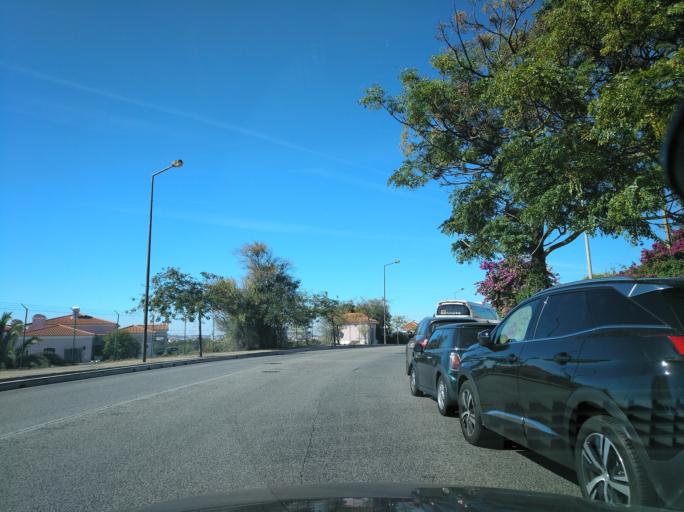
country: PT
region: Lisbon
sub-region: Loures
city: Moscavide
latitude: 38.7557
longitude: -9.1269
